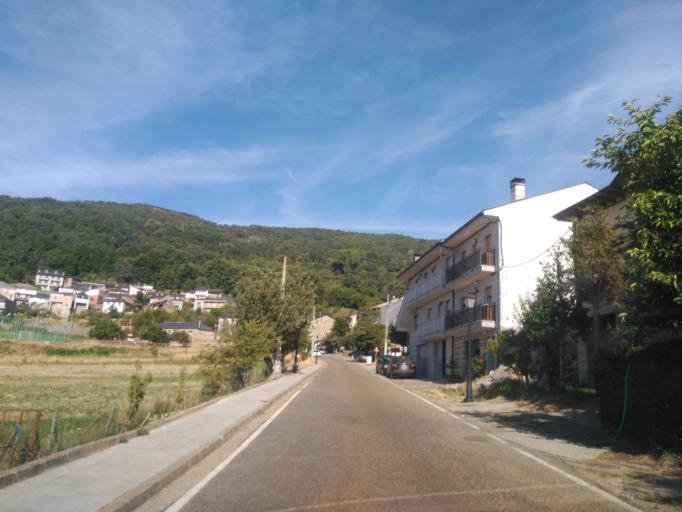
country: ES
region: Castille and Leon
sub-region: Provincia de Zamora
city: Galende
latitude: 42.1377
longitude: -6.7178
